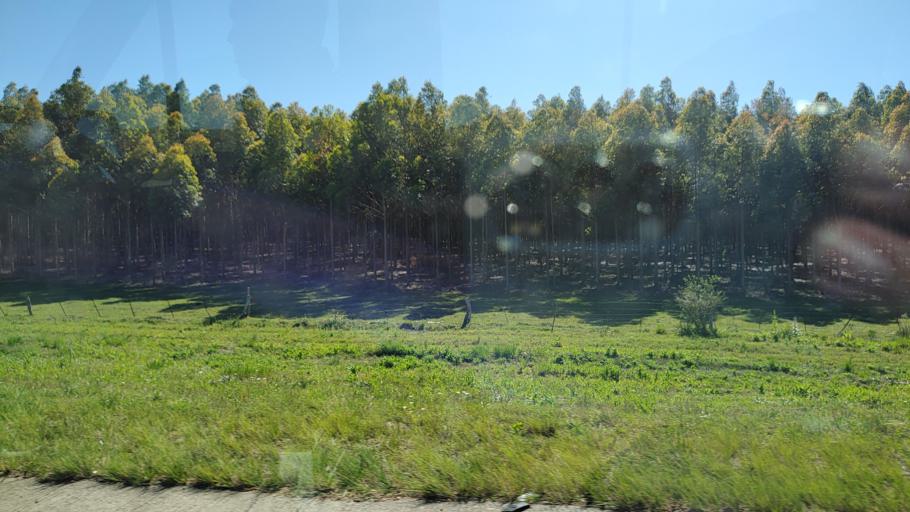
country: AR
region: Entre Rios
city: Villa Elisa
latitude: -32.0185
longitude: -58.2847
